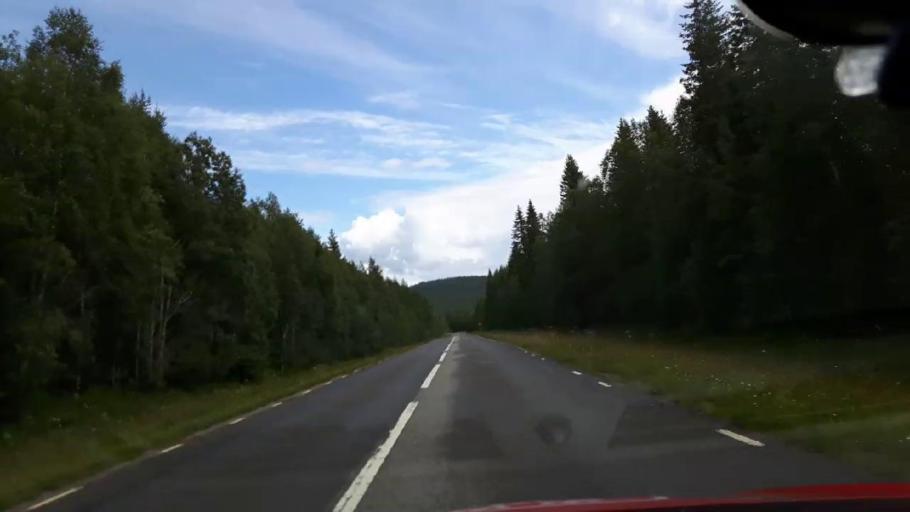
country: SE
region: Jaemtland
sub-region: Stroemsunds Kommun
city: Stroemsund
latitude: 64.3358
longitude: 14.9651
